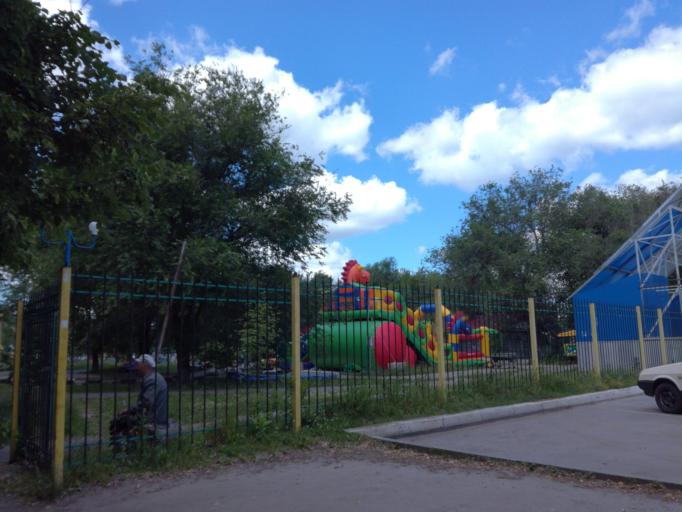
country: RU
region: Kursk
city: Kursk
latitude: 51.7467
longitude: 36.2525
